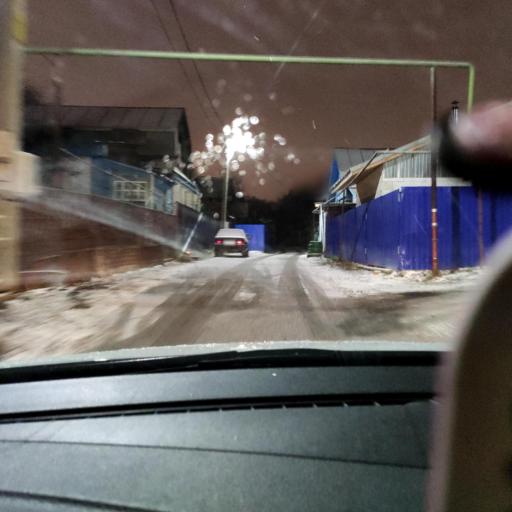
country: RU
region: Tatarstan
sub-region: Gorod Kazan'
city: Kazan
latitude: 55.7787
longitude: 49.1604
